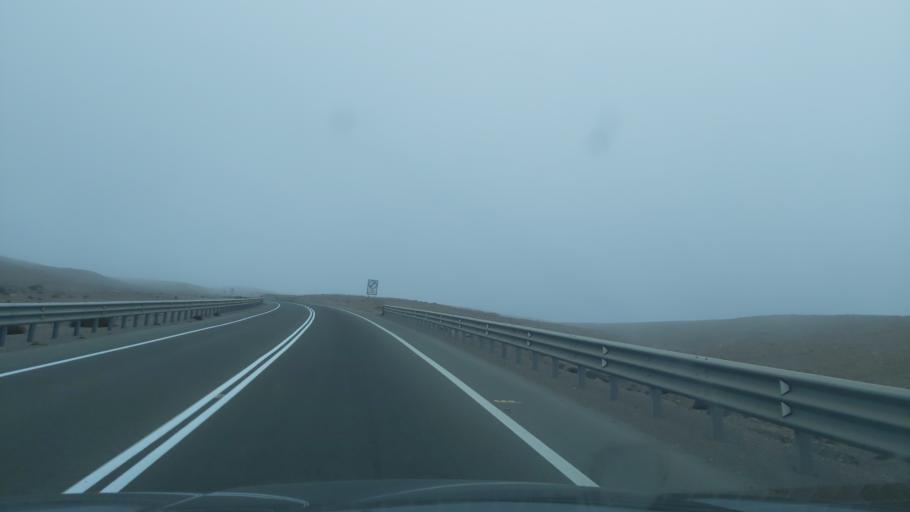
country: CL
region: Atacama
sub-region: Provincia de Copiapo
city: Copiapo
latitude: -27.2875
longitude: -70.1050
